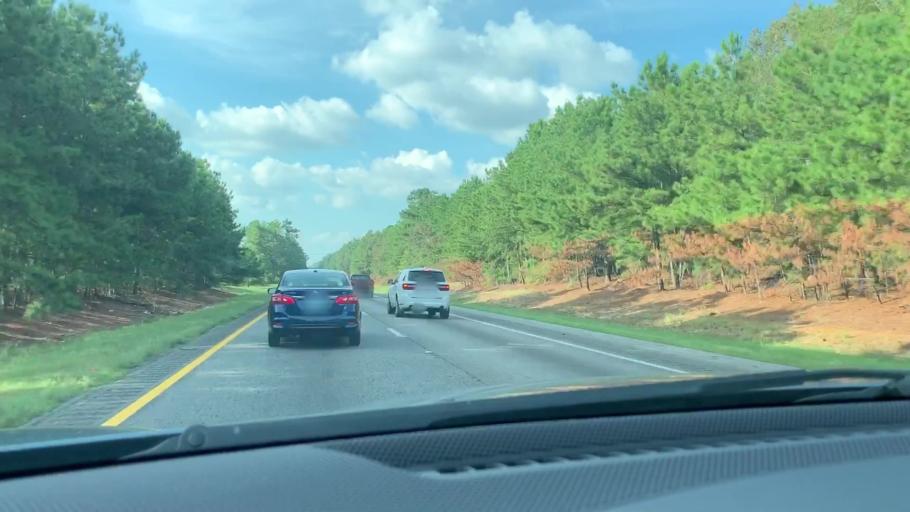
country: US
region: South Carolina
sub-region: Calhoun County
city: Saint Matthews
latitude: 33.6396
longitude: -80.8780
